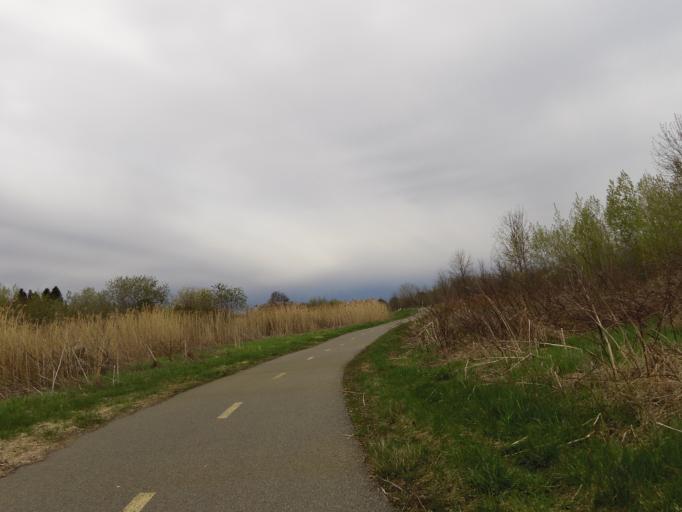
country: CA
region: Quebec
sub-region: Laurentides
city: Oka
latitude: 45.4681
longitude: -74.0710
